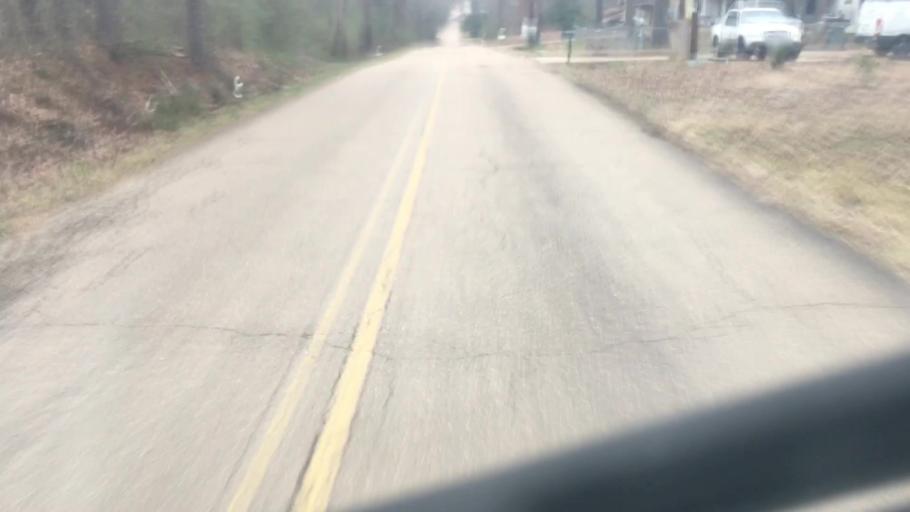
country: US
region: Alabama
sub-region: Walker County
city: Jasper
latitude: 33.8297
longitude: -87.2253
